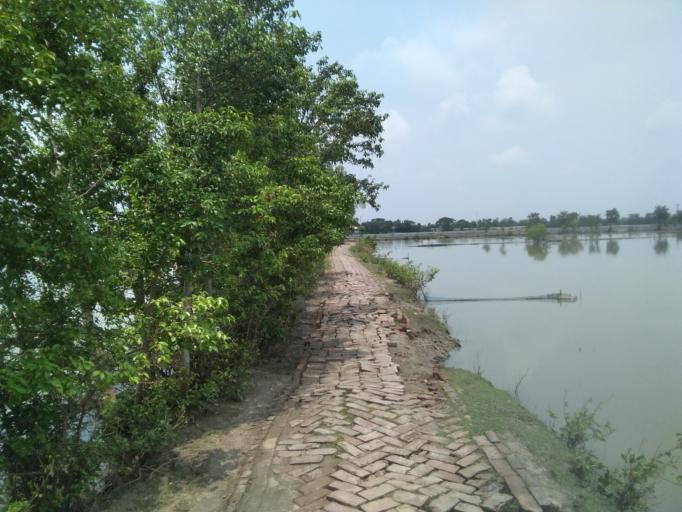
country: BD
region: Khulna
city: Phultala
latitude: 22.6397
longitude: 89.4037
